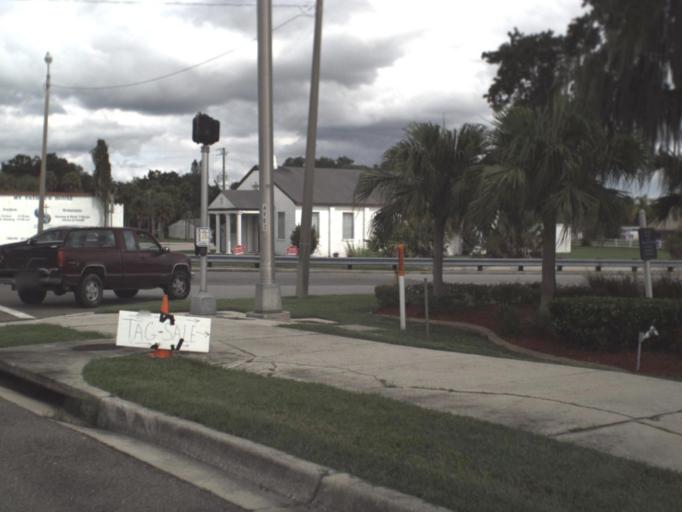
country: US
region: Florida
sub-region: Manatee County
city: Ellenton
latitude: 27.5350
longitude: -82.4921
